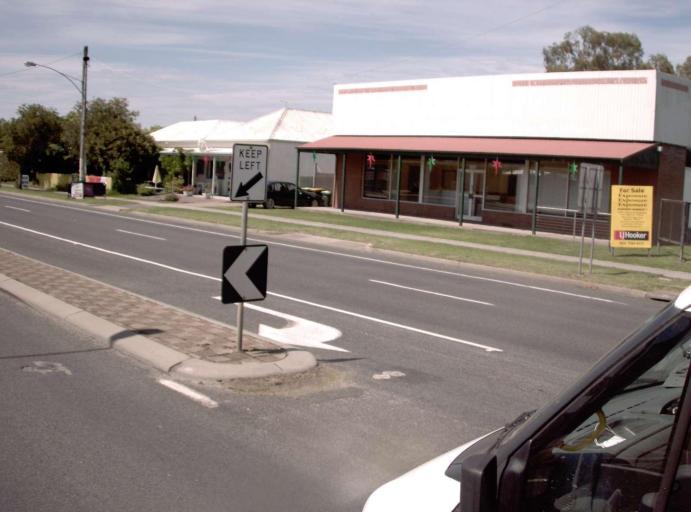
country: AU
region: Victoria
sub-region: Wellington
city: Sale
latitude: -37.9649
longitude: 147.0801
